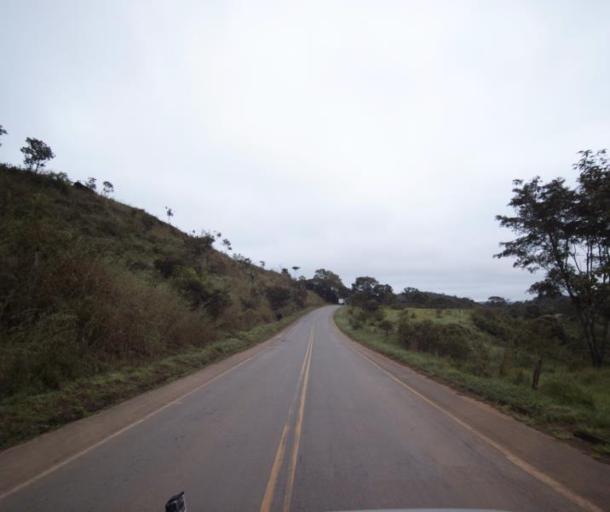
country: BR
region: Goias
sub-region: Pirenopolis
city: Pirenopolis
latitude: -15.9455
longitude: -48.8045
